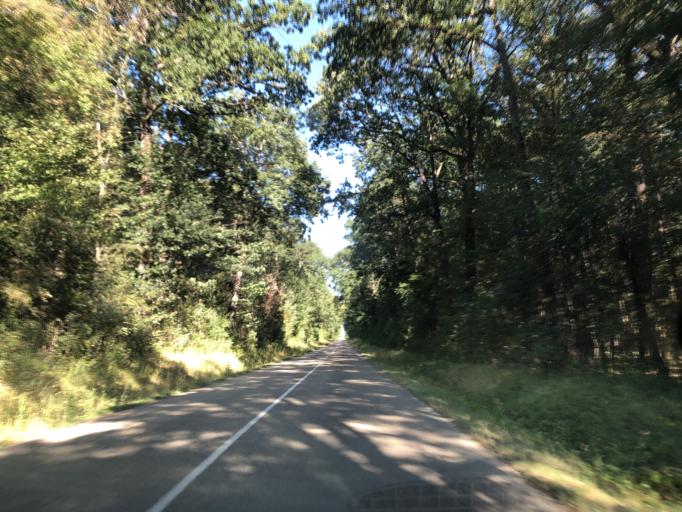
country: FR
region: Bourgogne
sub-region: Departement de l'Yonne
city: Gurgy
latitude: 47.8993
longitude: 3.5667
